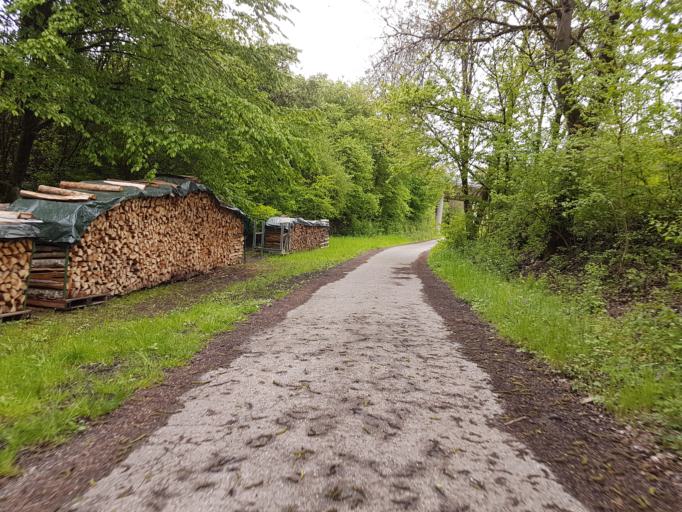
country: DE
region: Baden-Wuerttemberg
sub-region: Freiburg Region
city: Eggingen
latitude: 47.7160
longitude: 8.4256
